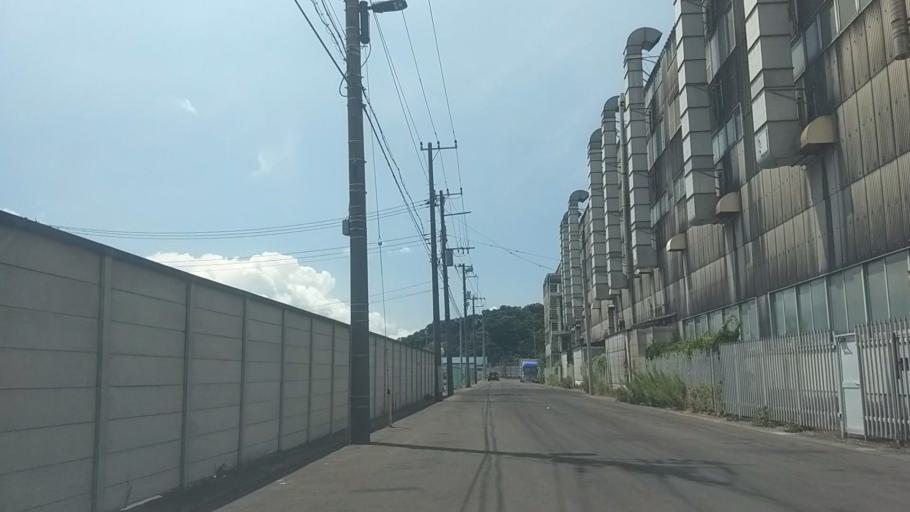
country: JP
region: Kanagawa
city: Yokosuka
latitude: 35.3093
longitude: 139.6422
